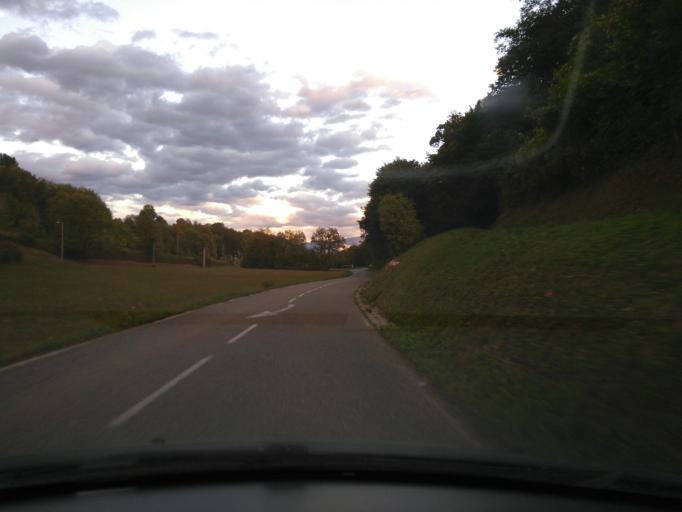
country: FR
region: Rhone-Alpes
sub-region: Departement de l'Isere
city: La Murette
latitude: 45.3681
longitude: 5.5307
